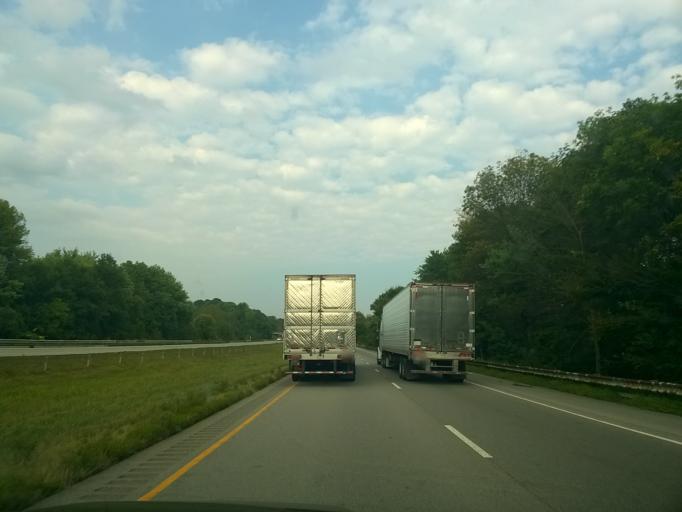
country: US
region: Indiana
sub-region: Putnam County
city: Cloverdale
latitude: 39.5043
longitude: -86.9503
